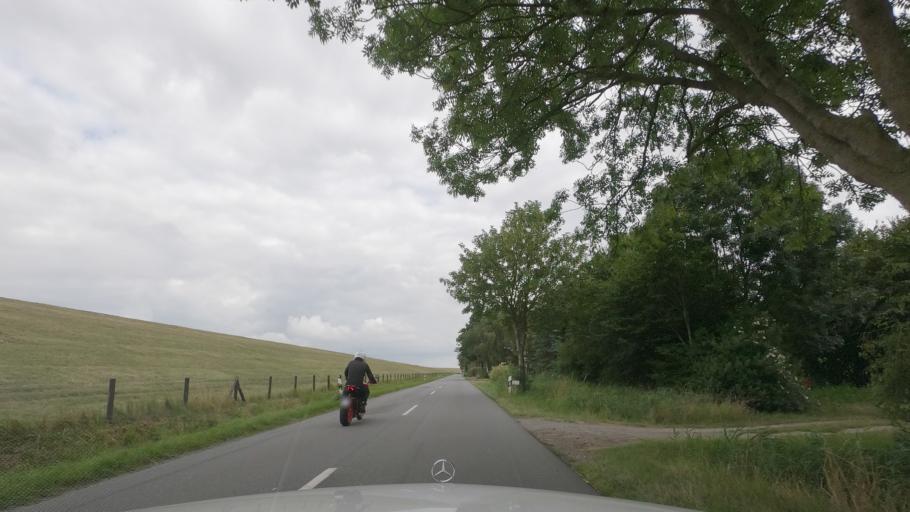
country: DE
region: Lower Saxony
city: Brake (Unterweser)
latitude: 53.3006
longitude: 8.5282
